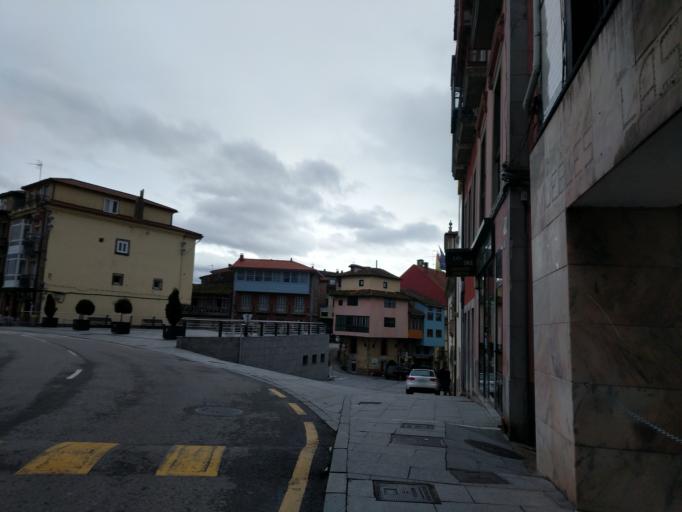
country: ES
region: Asturias
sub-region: Province of Asturias
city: Tineo
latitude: 43.3342
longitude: -6.4168
